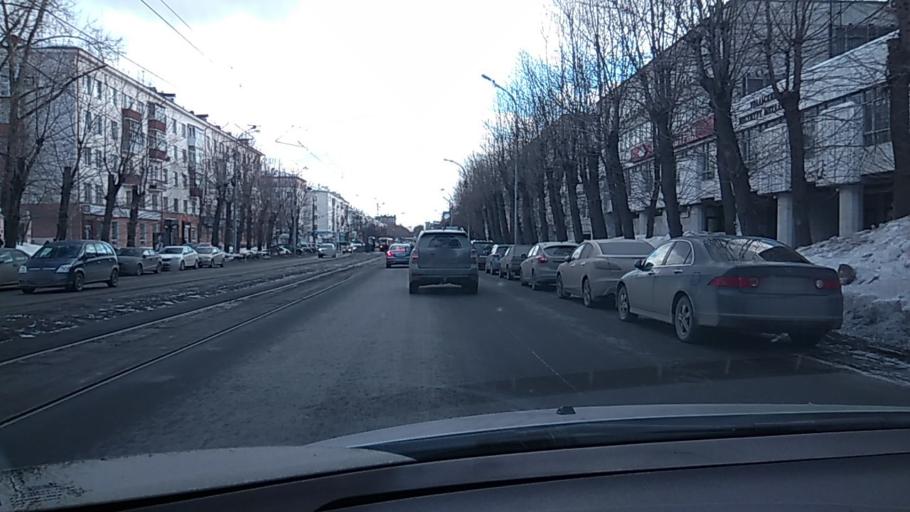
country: RU
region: Sverdlovsk
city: Yekaterinburg
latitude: 56.8448
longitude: 60.6447
